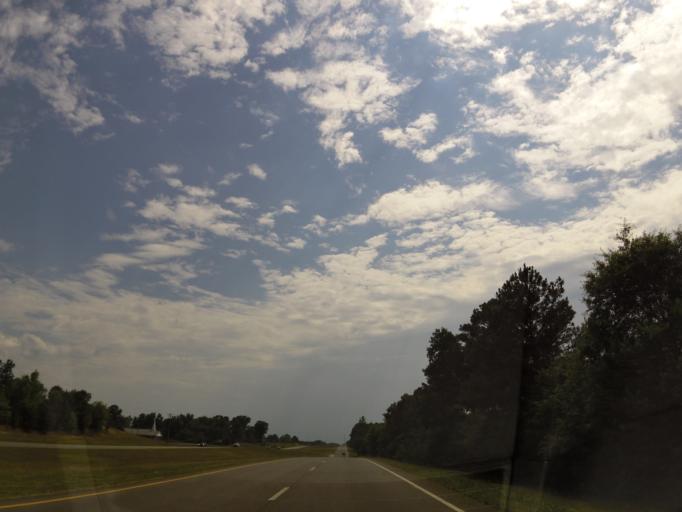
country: US
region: Alabama
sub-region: Jackson County
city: Stevenson
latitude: 34.8114
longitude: -85.8577
